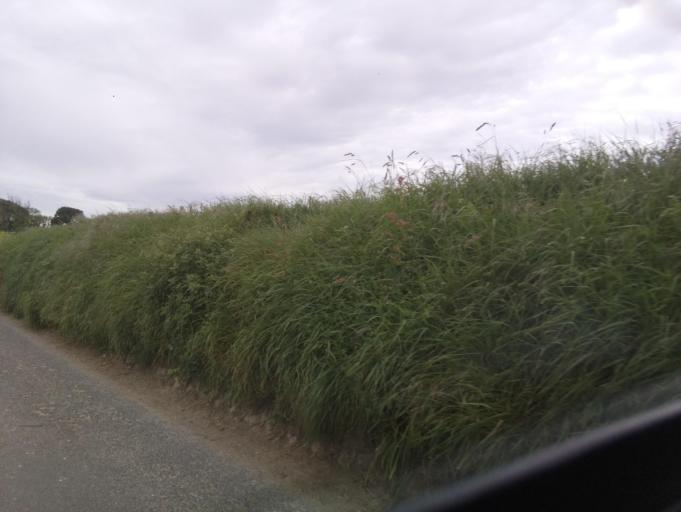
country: GB
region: England
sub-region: Devon
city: Dartmouth
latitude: 50.3484
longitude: -3.6581
